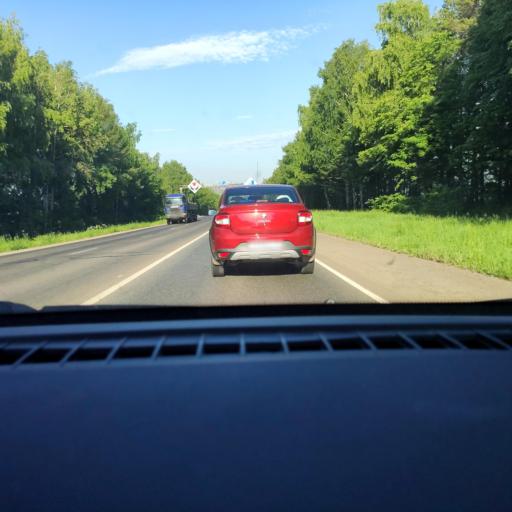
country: RU
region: Udmurtiya
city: Khokhryaki
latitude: 56.9148
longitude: 53.4089
